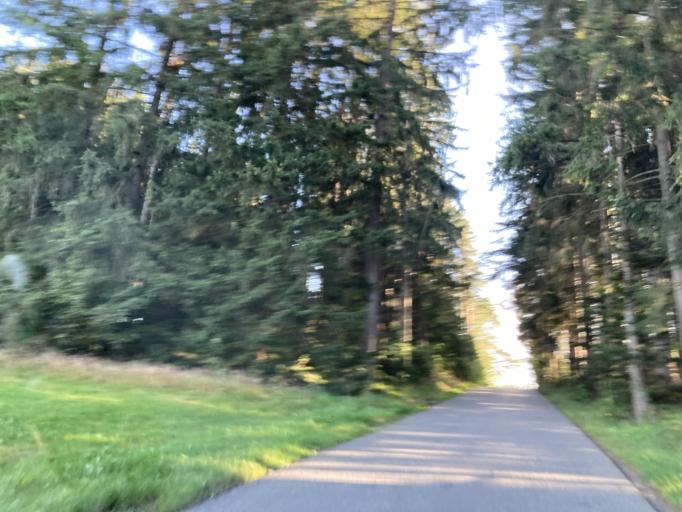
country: DE
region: Baden-Wuerttemberg
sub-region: Freiburg Region
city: Sankt Georgen im Schwarzwald
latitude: 48.1471
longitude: 8.2857
